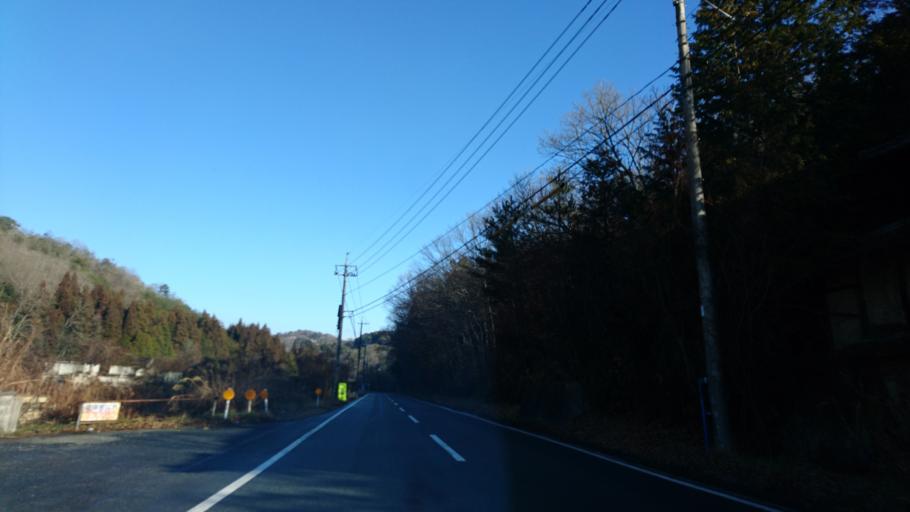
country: JP
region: Okayama
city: Takahashi
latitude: 34.8147
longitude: 133.6747
